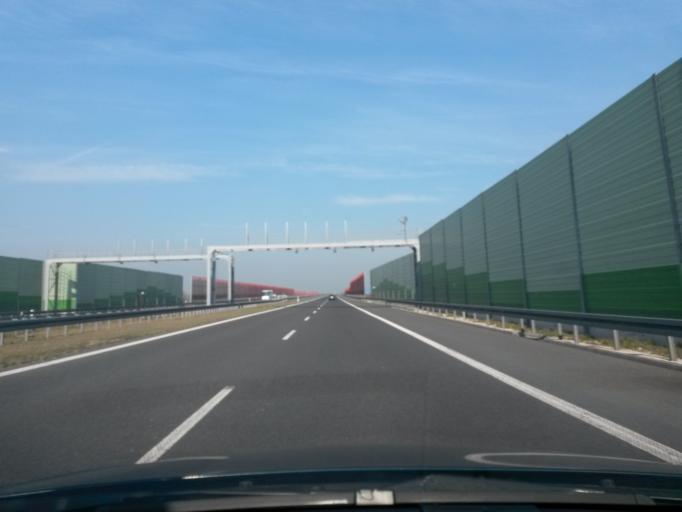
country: PL
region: Lodz Voivodeship
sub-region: Powiat leczycki
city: Piatek
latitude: 52.1271
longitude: 19.4939
